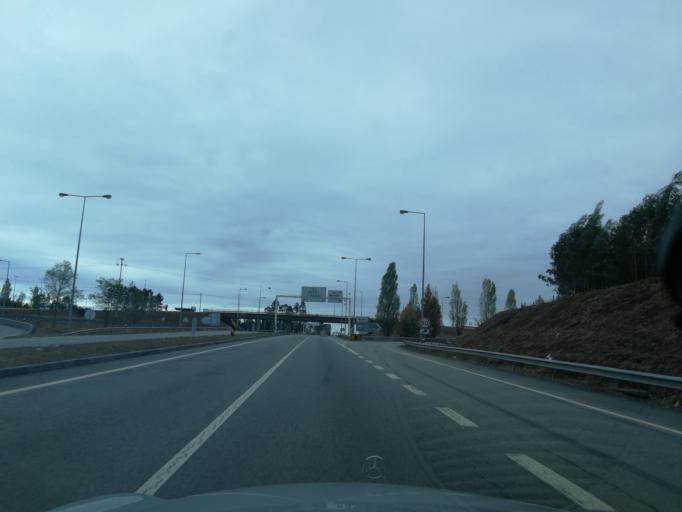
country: PT
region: Aveiro
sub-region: Agueda
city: Valongo
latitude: 40.5971
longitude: -8.4686
